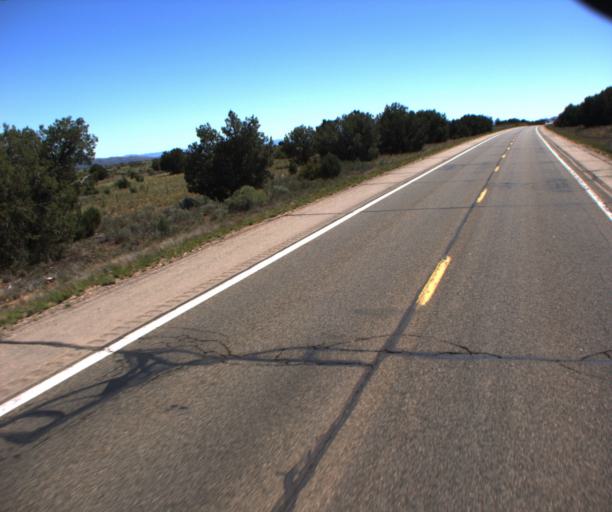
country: US
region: Arizona
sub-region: Yavapai County
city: Paulden
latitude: 34.9608
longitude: -112.4150
